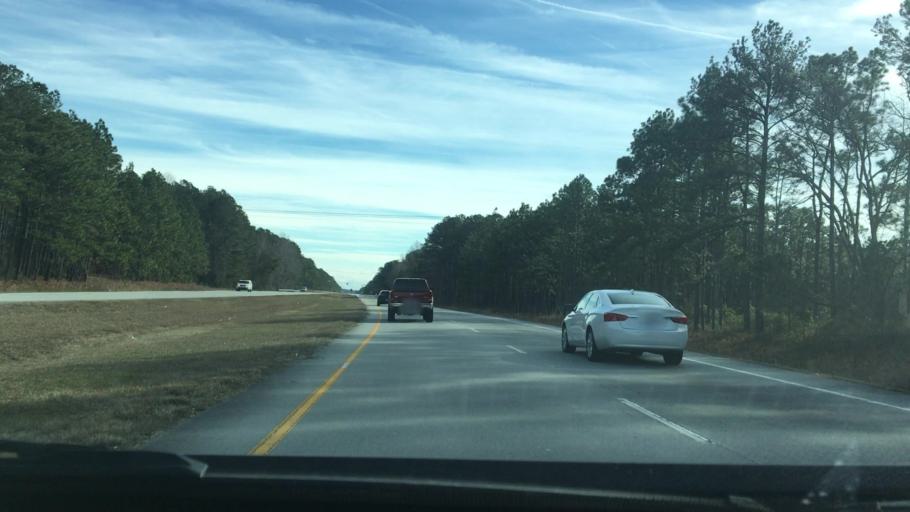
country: US
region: North Carolina
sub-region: Carteret County
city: Newport
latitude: 34.7743
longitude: -76.8699
